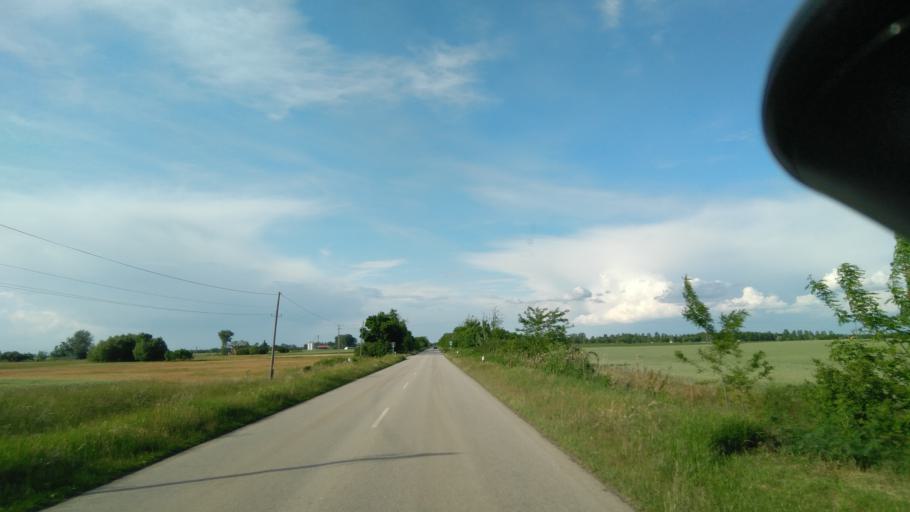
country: HU
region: Bekes
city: Elek
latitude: 46.5685
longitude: 21.2668
